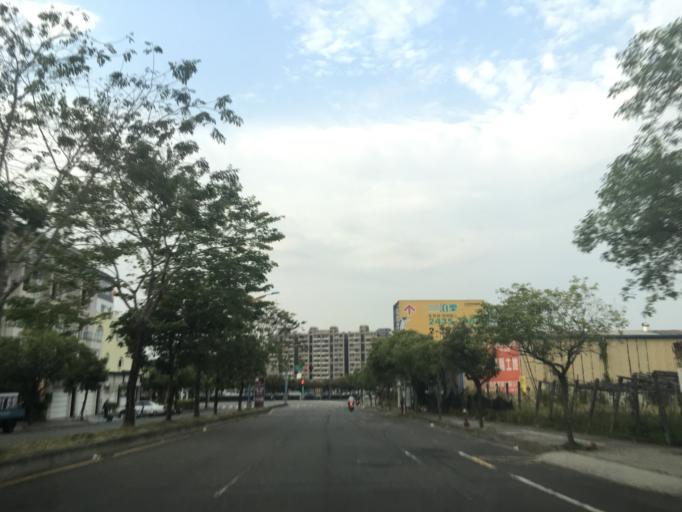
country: TW
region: Taiwan
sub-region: Taichung City
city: Taichung
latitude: 24.1749
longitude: 120.7305
